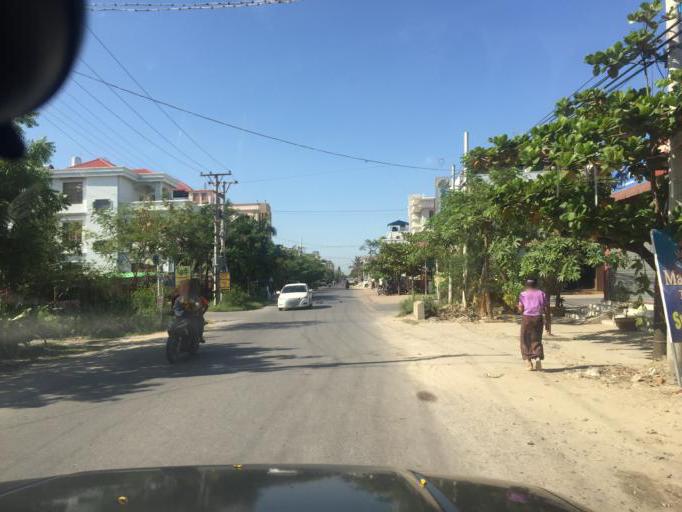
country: MM
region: Mandalay
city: Mandalay
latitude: 21.9592
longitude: 96.1100
